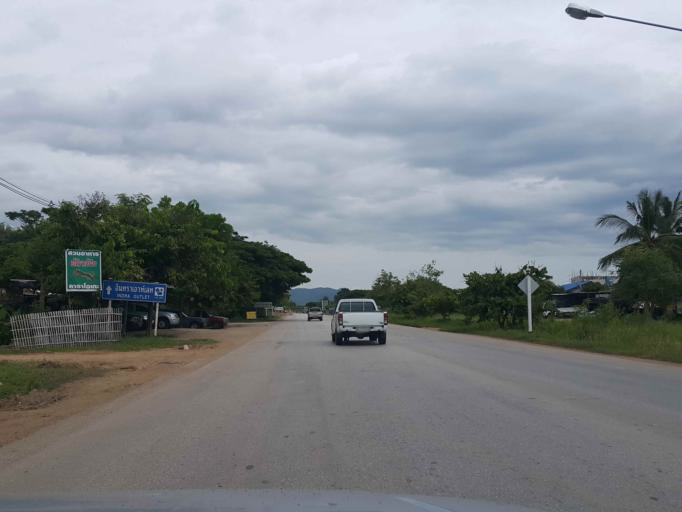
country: TH
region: Lampang
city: Lampang
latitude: 18.2618
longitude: 99.4705
